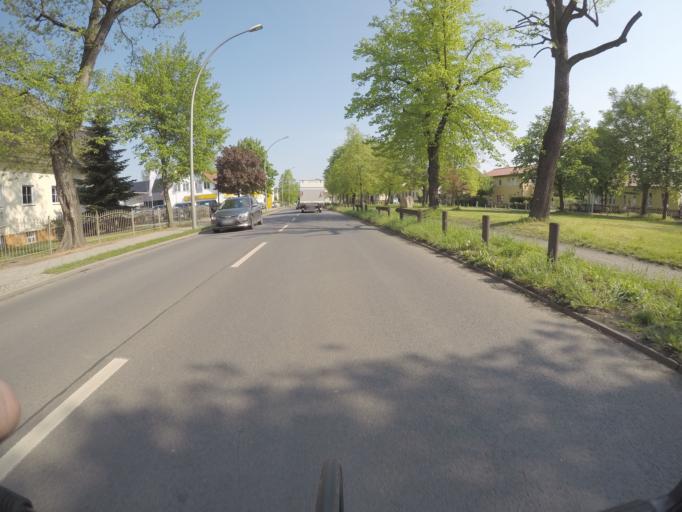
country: DE
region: Berlin
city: Buchholz
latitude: 52.6087
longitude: 13.4339
